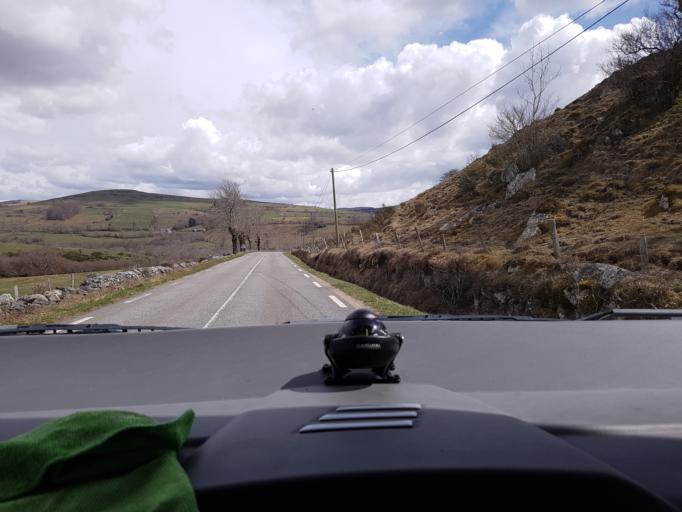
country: FR
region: Midi-Pyrenees
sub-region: Departement de l'Aveyron
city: Laguiole
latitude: 44.7040
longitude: 2.8587
